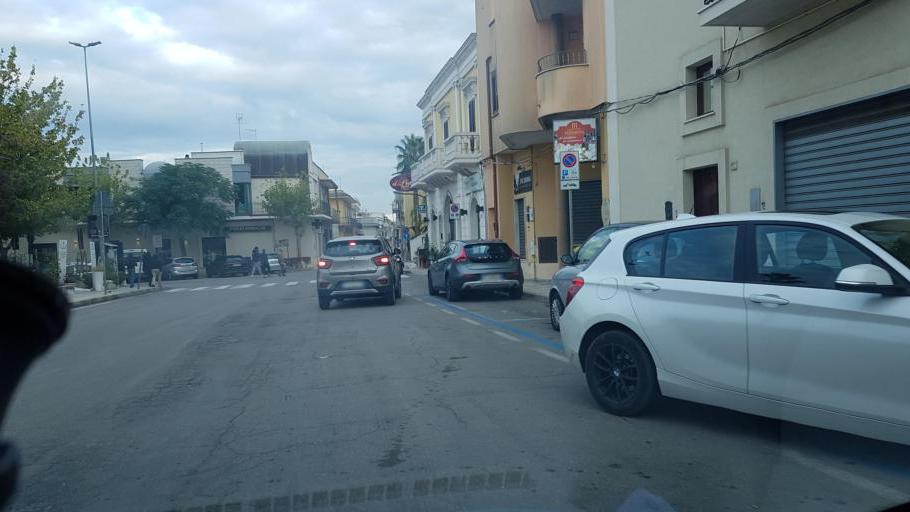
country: IT
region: Apulia
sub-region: Provincia di Brindisi
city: Oria
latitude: 40.5017
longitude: 17.6413
